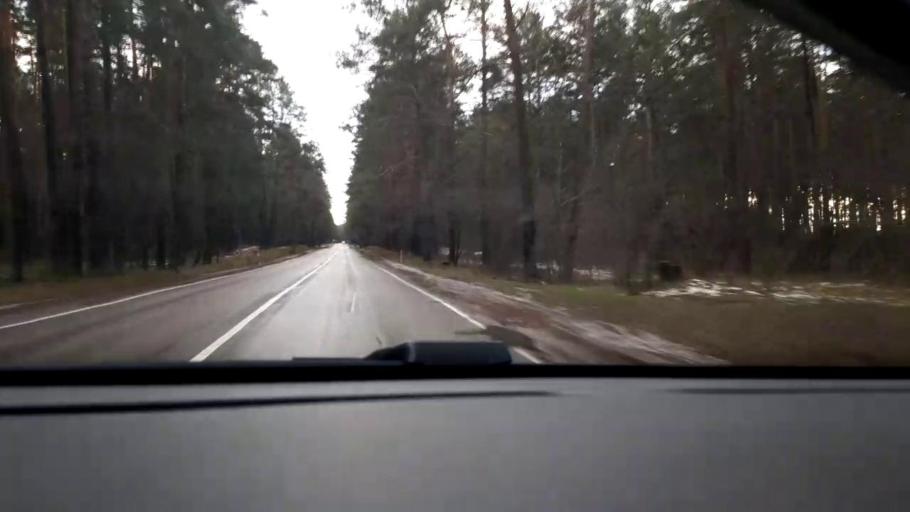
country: LT
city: Nemencine
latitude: 54.7815
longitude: 25.3838
